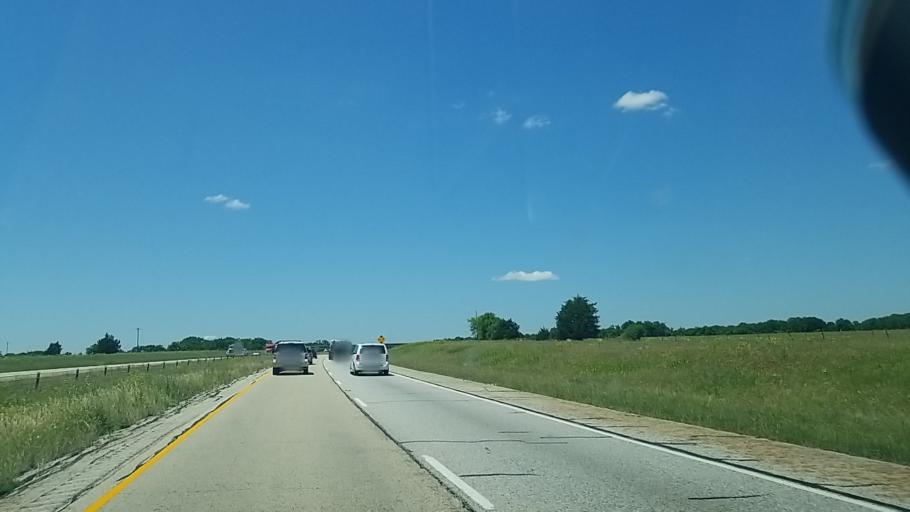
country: US
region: Texas
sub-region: Leon County
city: Centerville
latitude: 31.1207
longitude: -95.9747
